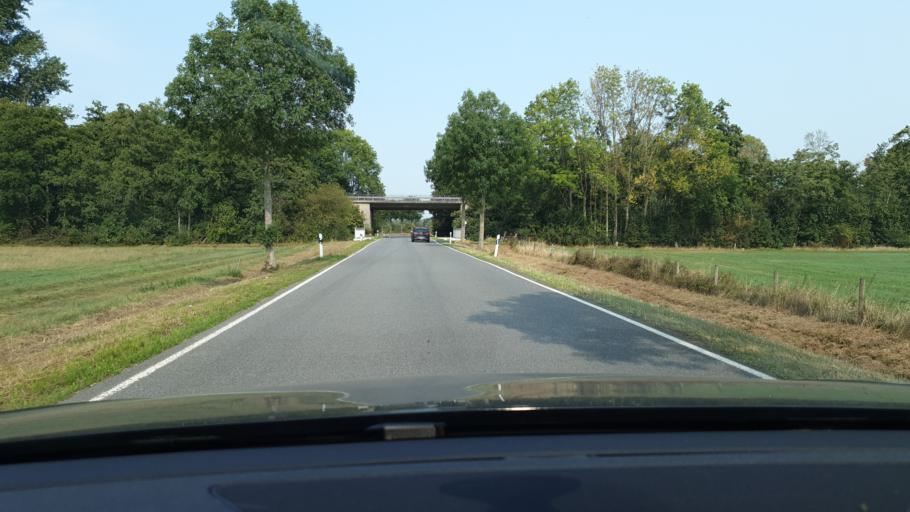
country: DE
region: North Rhine-Westphalia
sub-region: Regierungsbezirk Dusseldorf
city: Kranenburg
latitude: 51.7994
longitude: 6.0149
